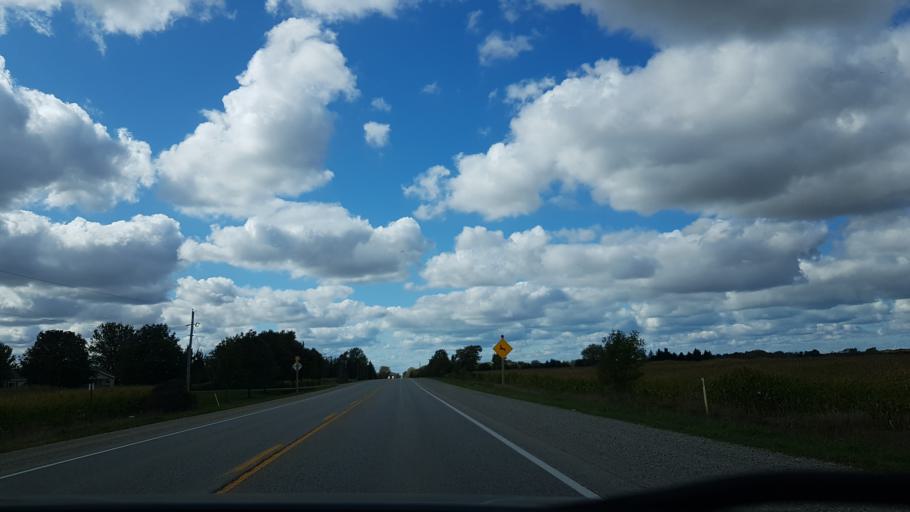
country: CA
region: Ontario
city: South Huron
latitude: 43.3589
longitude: -81.5109
